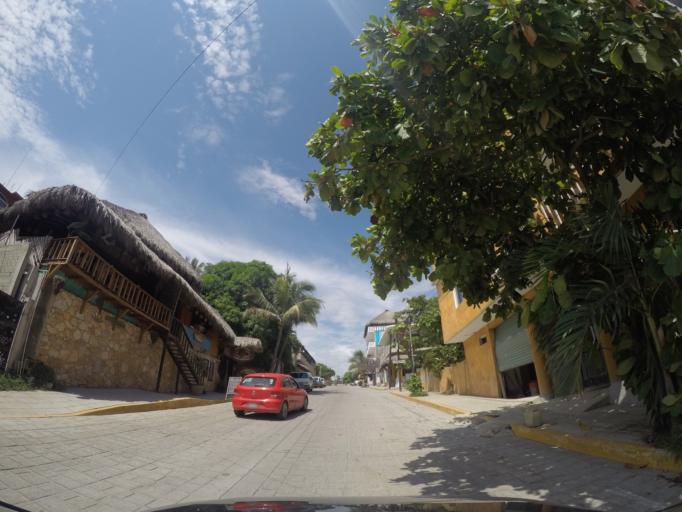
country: MX
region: Oaxaca
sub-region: Santa Maria Colotepec
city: Brisas de Zicatela
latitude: 15.8512
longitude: -97.0536
